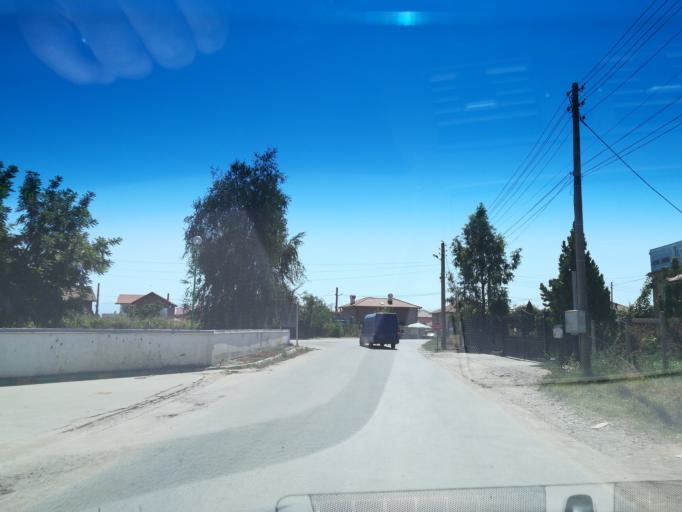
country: BG
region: Pazardzhik
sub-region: Obshtina Pazardzhik
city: Pazardzhik
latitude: 42.2721
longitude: 24.3966
